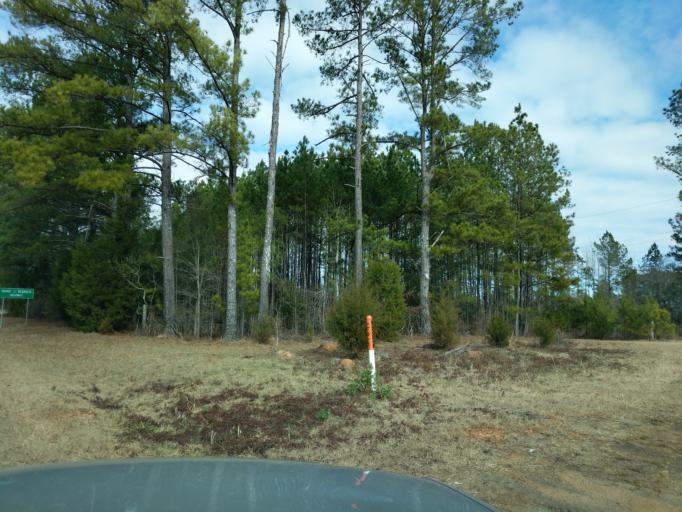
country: US
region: South Carolina
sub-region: Edgefield County
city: Edgefield
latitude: 33.8713
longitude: -81.9952
